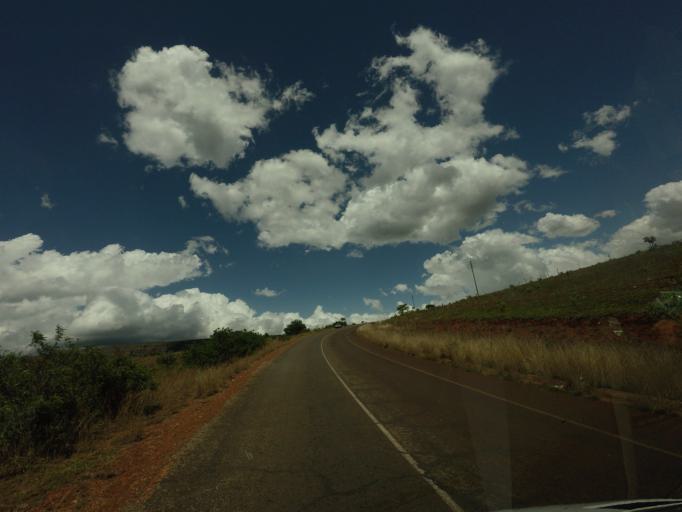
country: ZA
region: Mpumalanga
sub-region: Ehlanzeni District
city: Graksop
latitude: -24.6392
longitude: 30.8139
